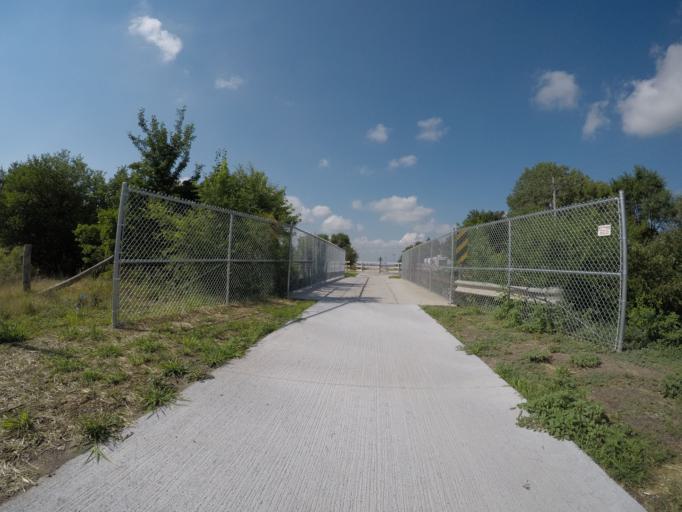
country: US
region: Nebraska
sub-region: Buffalo County
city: Kearney
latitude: 40.6728
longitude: -99.0277
